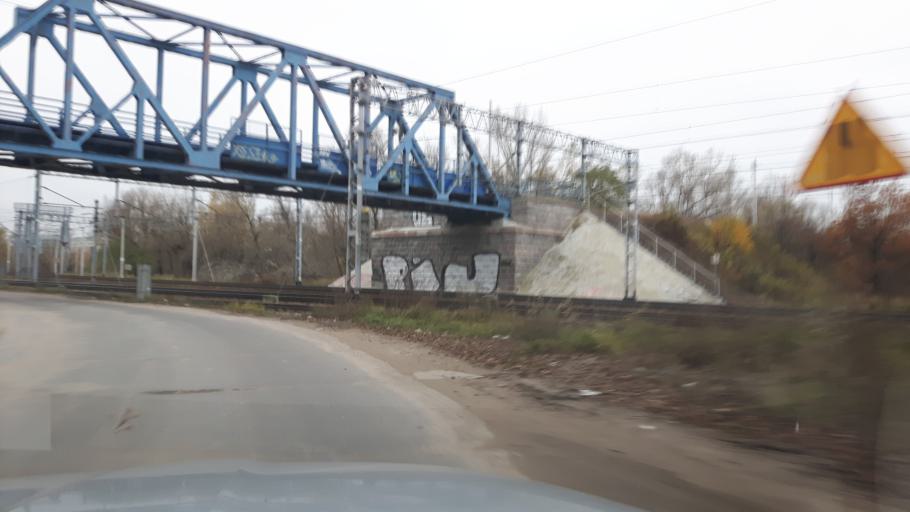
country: PL
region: Masovian Voivodeship
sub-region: Warszawa
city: Praga Polnoc
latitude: 52.2709
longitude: 21.0274
